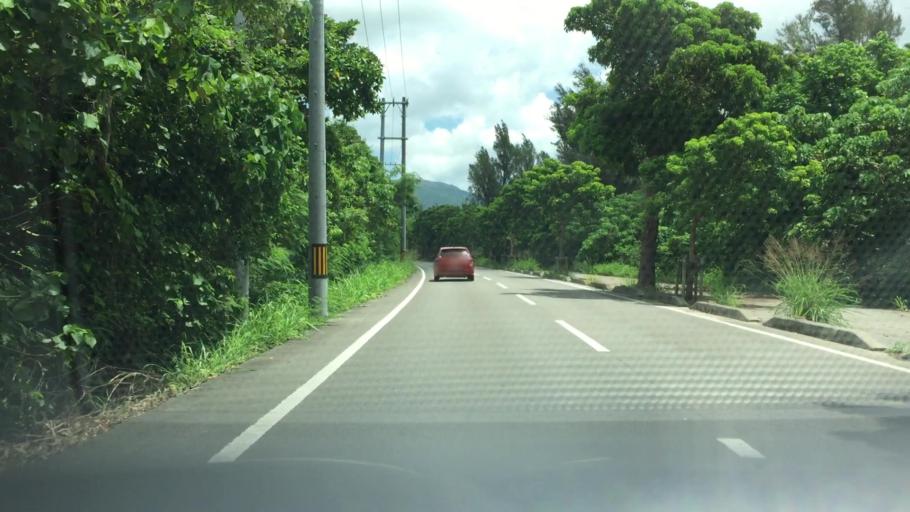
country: JP
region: Okinawa
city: Ishigaki
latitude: 24.3849
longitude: 124.1373
